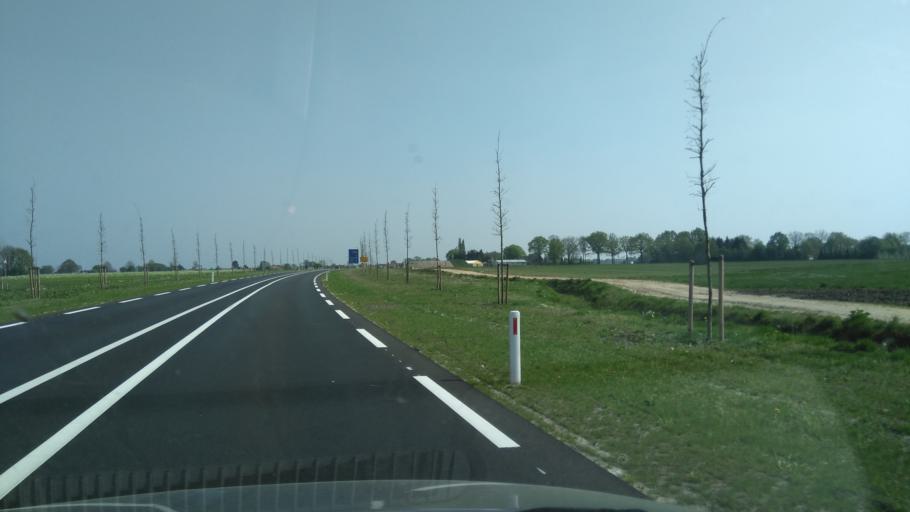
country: NL
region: North Brabant
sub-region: Gemeente Baarle-Nassau
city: Baarle-Nassau
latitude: 51.4553
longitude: 4.9383
